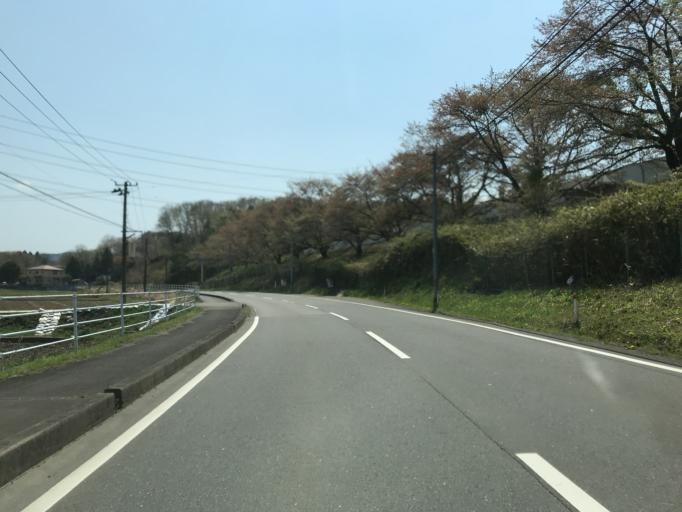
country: JP
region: Fukushima
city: Ishikawa
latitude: 37.0749
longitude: 140.4208
